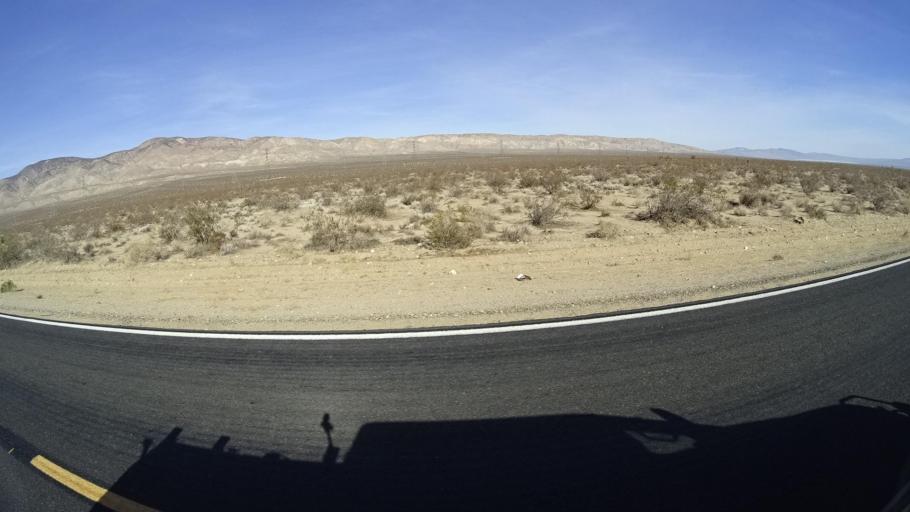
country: US
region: California
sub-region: Kern County
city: Mojave
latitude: 35.1247
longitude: -118.1479
